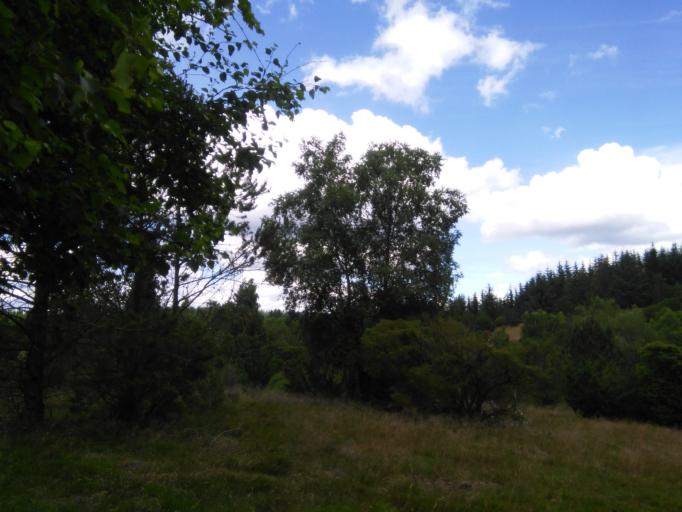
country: DK
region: Central Jutland
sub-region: Silkeborg Kommune
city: Virklund
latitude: 56.0691
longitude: 9.4446
